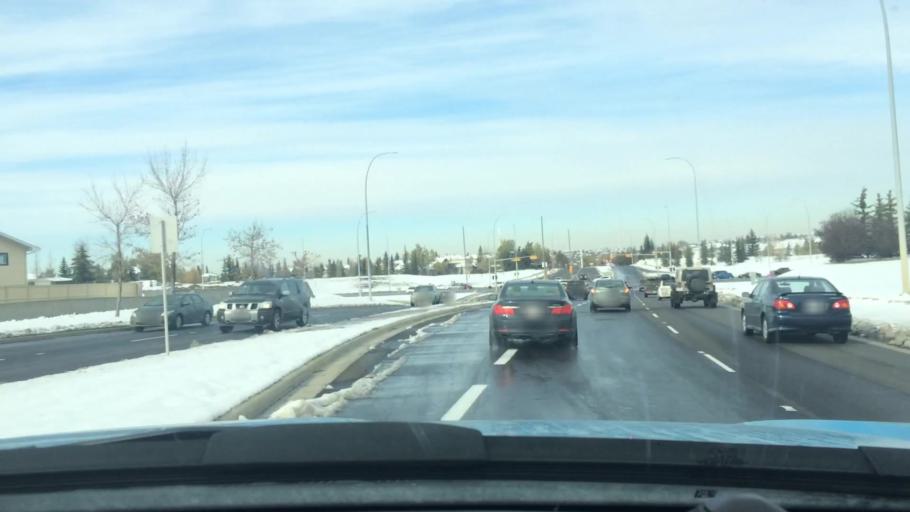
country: CA
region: Alberta
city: Calgary
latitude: 51.1417
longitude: -114.1088
